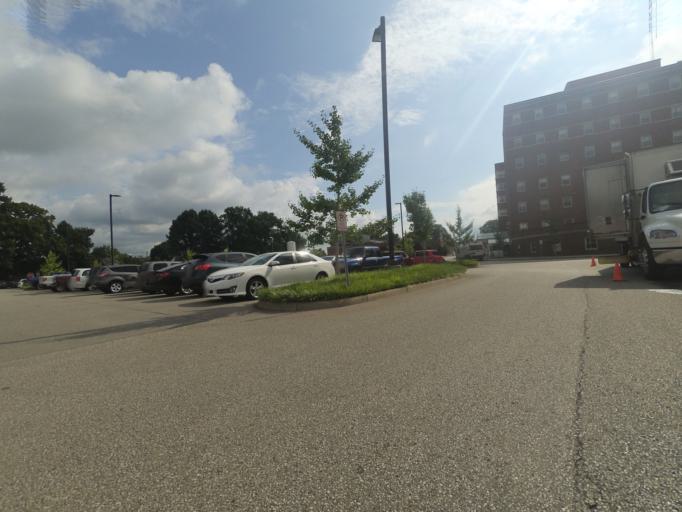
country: US
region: West Virginia
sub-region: Cabell County
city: Huntington
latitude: 38.4327
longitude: -82.4017
